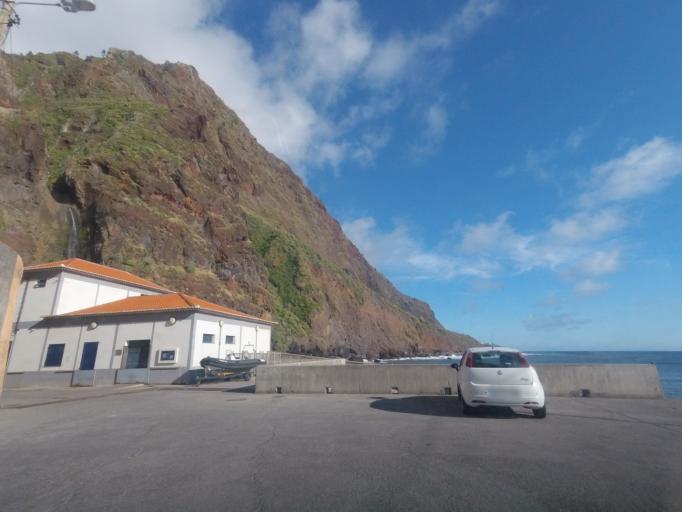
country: PT
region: Madeira
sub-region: Calheta
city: Faja da Ovelha
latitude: 32.7525
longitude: -17.2242
